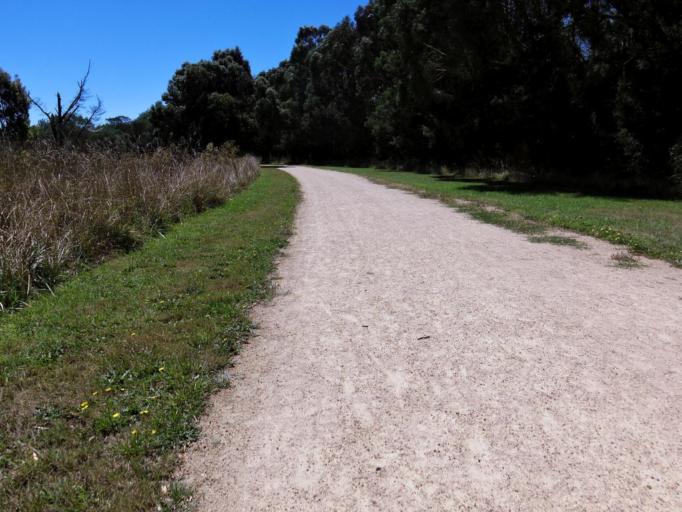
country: AU
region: Victoria
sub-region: Hume
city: Sunbury
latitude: -37.3510
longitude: 144.5251
